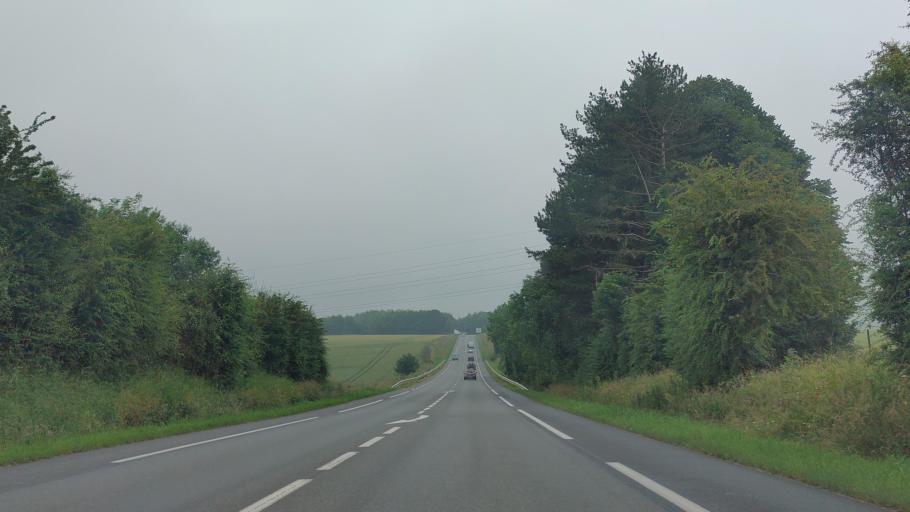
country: FR
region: Picardie
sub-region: Departement de la Somme
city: Fressenneville
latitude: 50.0740
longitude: 1.5698
